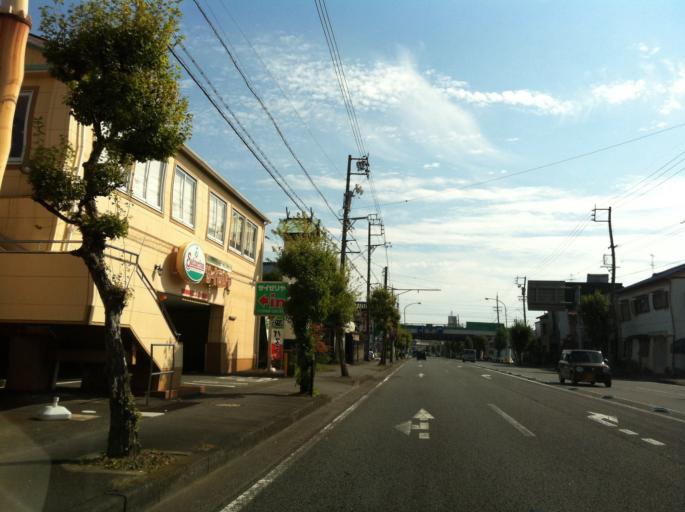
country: JP
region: Shizuoka
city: Shizuoka-shi
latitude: 35.0323
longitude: 138.4775
